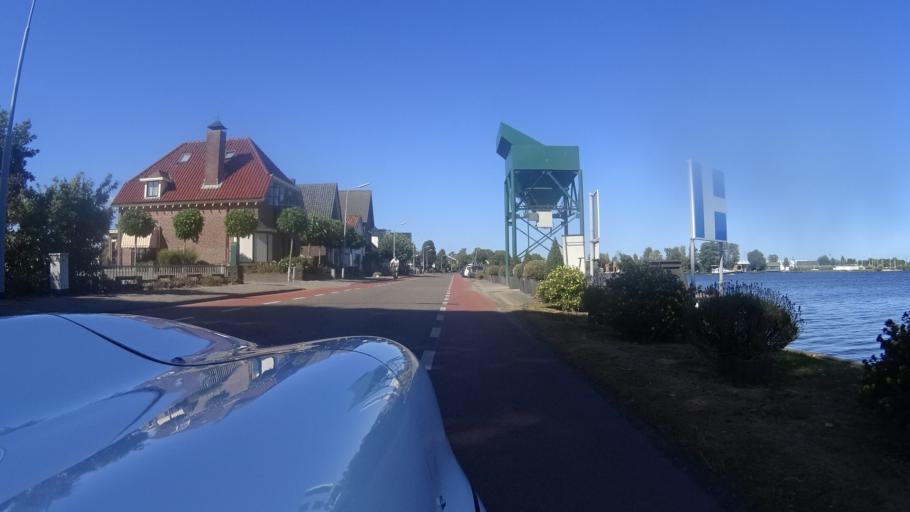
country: NL
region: North Holland
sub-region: Gemeente Aalsmeer
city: Aalsmeer
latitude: 52.2539
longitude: 4.7110
